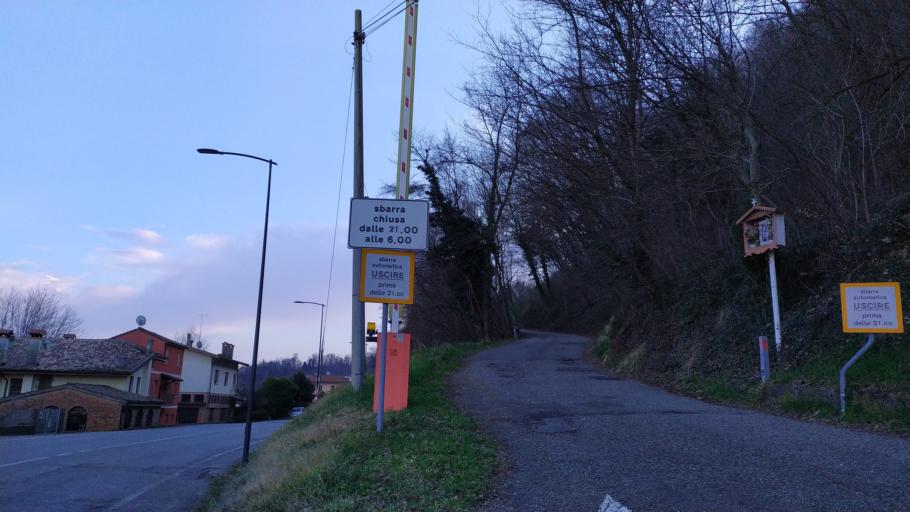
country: IT
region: Veneto
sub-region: Provincia di Treviso
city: Cornuda
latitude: 45.8385
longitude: 11.9931
